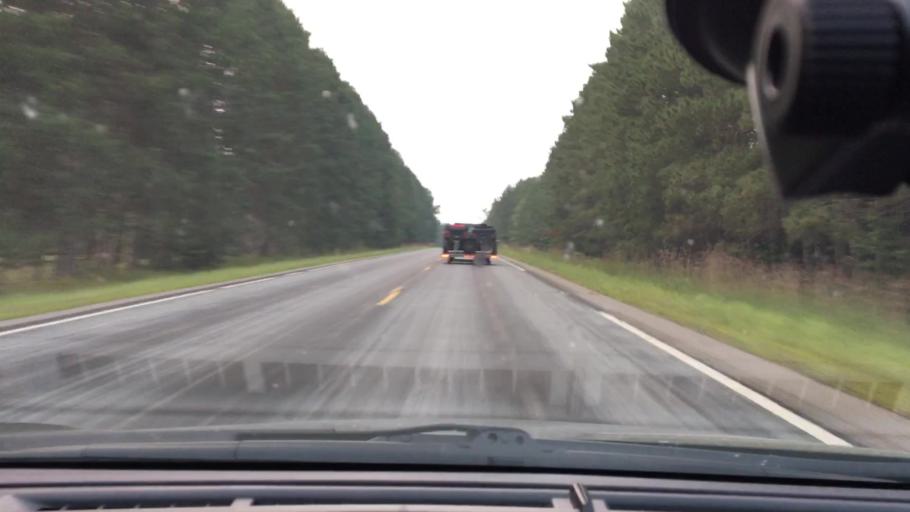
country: US
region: Minnesota
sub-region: Crow Wing County
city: Cross Lake
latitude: 46.7662
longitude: -93.9664
